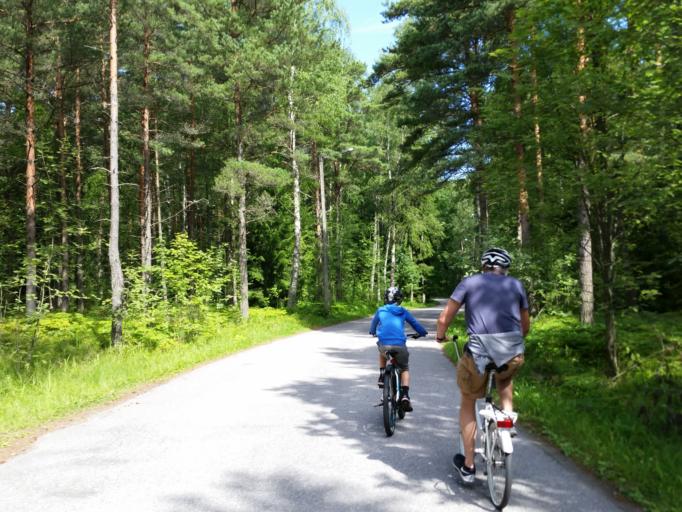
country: FI
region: Uusimaa
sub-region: Raaseporin
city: Hanko
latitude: 59.8290
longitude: 22.9288
